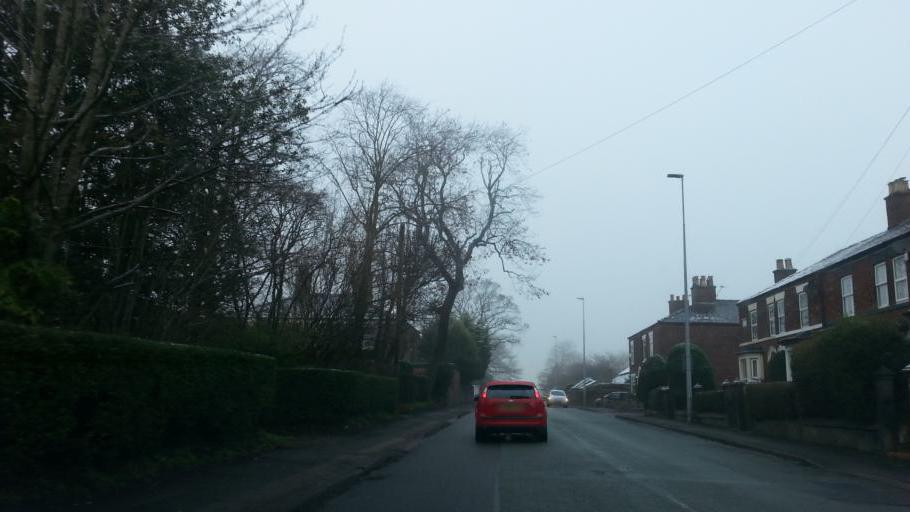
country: GB
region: England
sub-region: Cheshire East
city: Congleton
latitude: 53.1557
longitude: -2.1888
